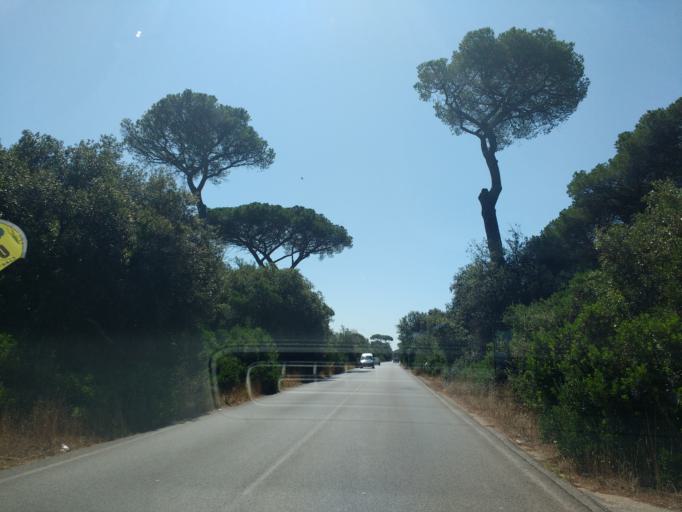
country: IT
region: Latium
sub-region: Citta metropolitana di Roma Capitale
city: Acilia-Castel Fusano-Ostia Antica
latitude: 41.7196
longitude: 12.3489
